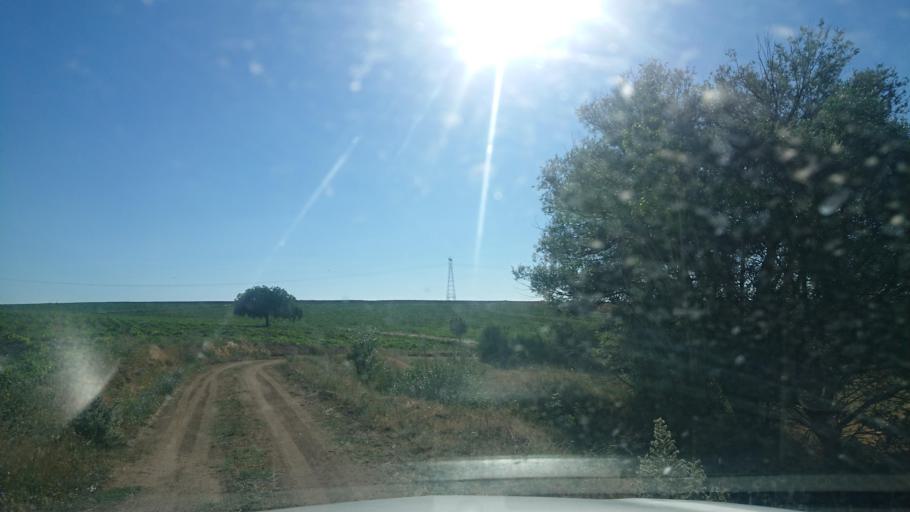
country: TR
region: Aksaray
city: Agacoren
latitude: 38.8332
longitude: 33.9410
